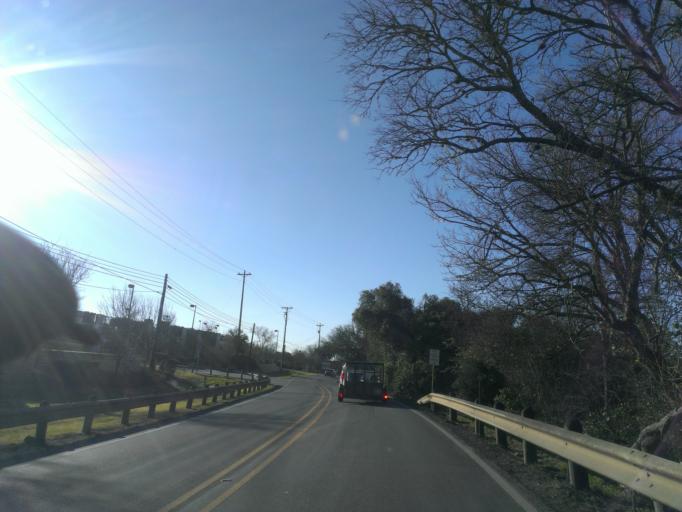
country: US
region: Texas
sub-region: Hays County
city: Dripping Springs
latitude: 30.1902
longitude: -98.0875
